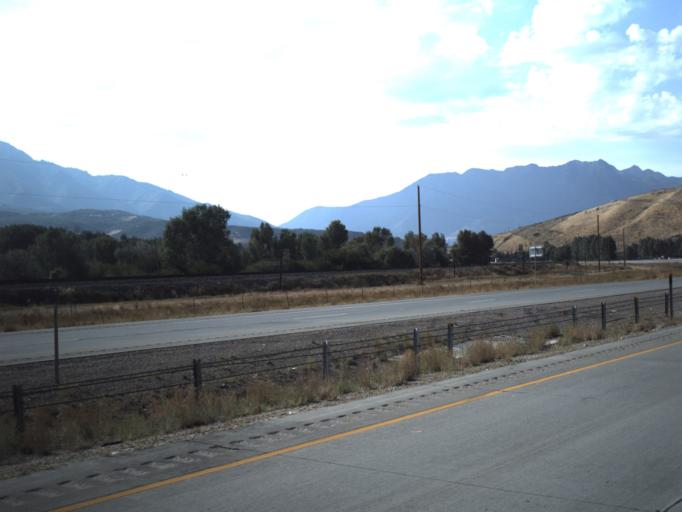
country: US
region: Utah
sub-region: Morgan County
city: Mountain Green
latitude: 41.1075
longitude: -111.7483
